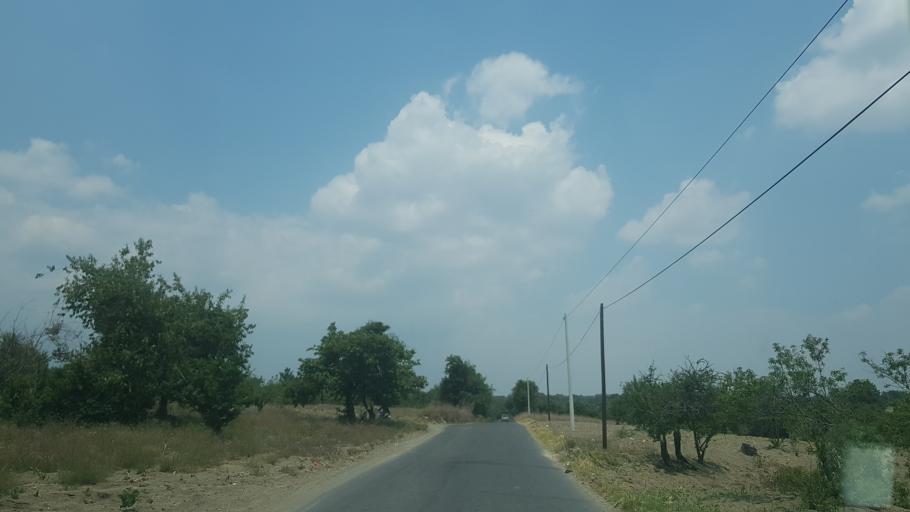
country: MX
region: Puebla
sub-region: San Nicolas de los Ranchos
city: San Pedro Yancuitlalpan
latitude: 19.0883
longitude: -98.4823
